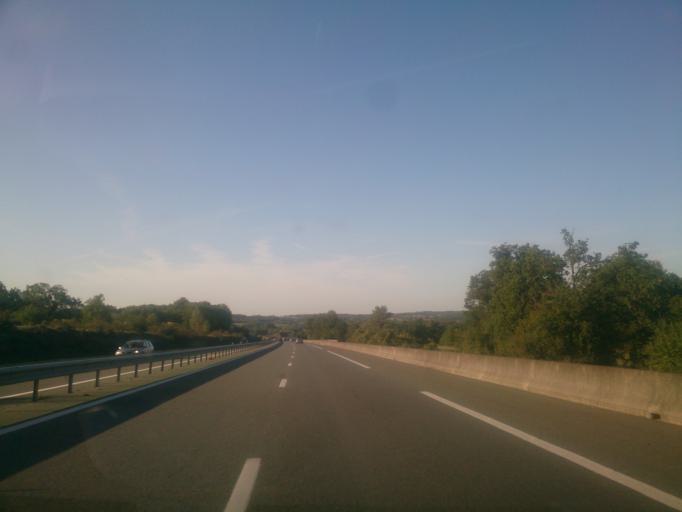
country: FR
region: Midi-Pyrenees
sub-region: Departement du Lot
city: Le Vigan
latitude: 44.6785
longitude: 1.5716
